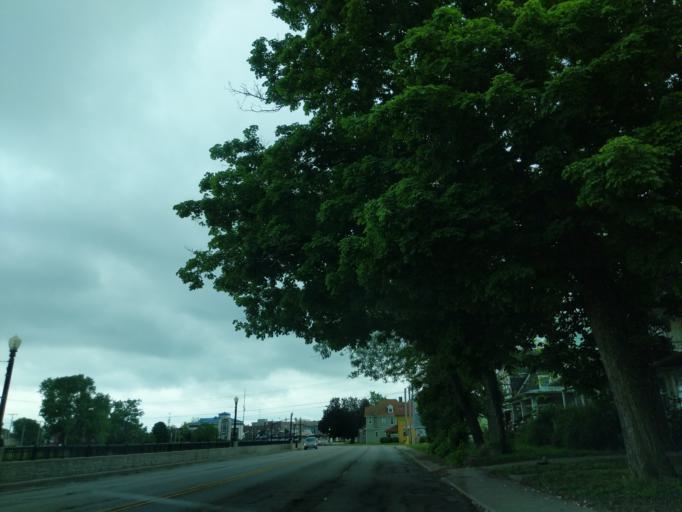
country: US
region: Indiana
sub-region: Delaware County
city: Muncie
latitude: 40.1989
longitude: -85.3909
